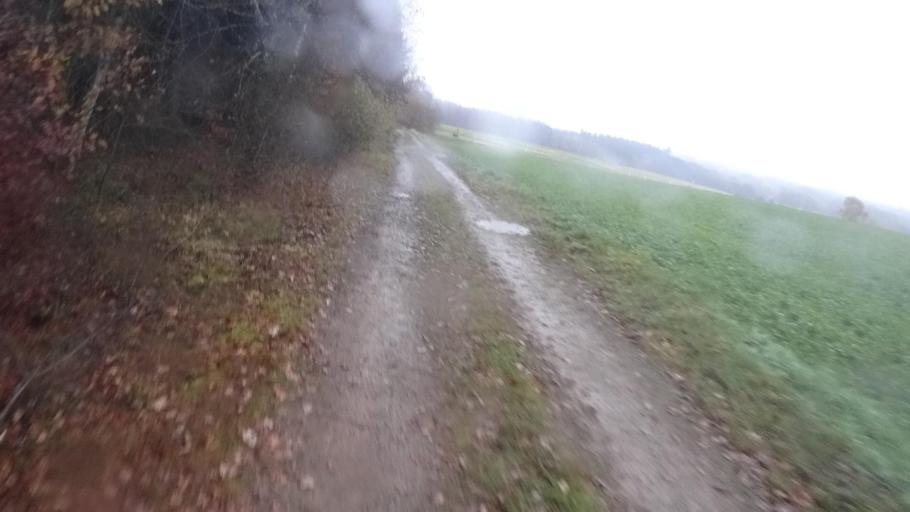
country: DE
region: Rheinland-Pfalz
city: Maisborn
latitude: 50.0795
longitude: 7.5919
